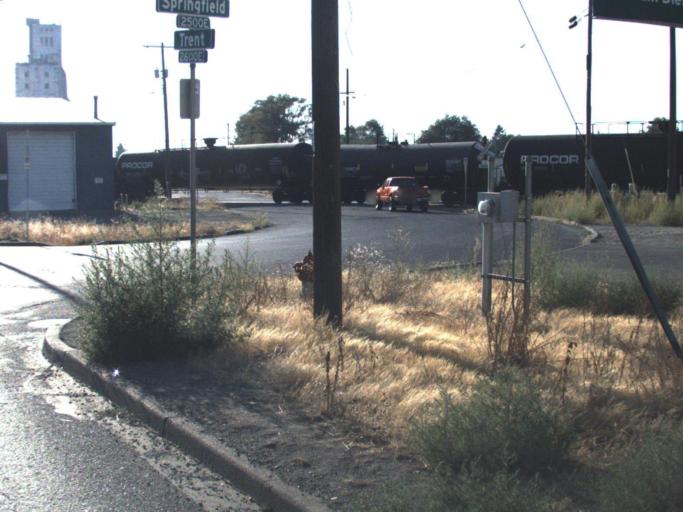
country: US
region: Washington
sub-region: Spokane County
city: Spokane
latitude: 47.6631
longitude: -117.3719
